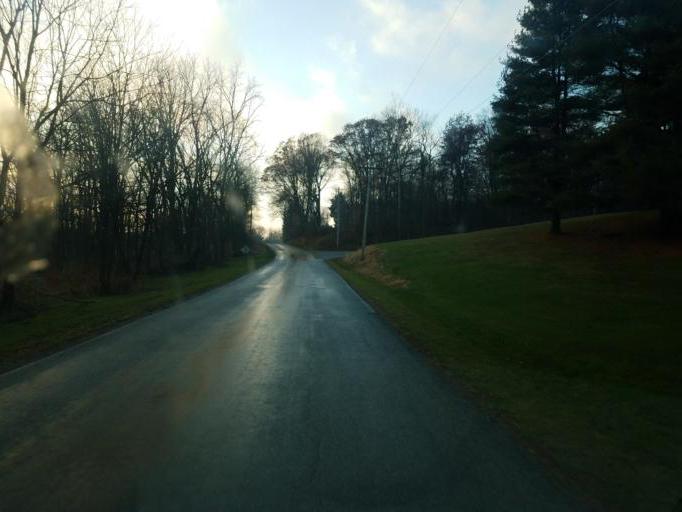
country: US
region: Ohio
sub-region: Knox County
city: Centerburg
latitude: 40.2409
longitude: -82.6634
